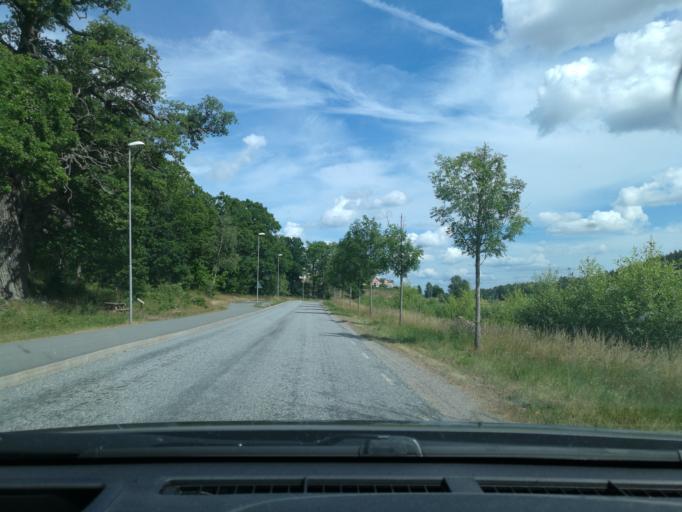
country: SE
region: Stockholm
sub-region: Sigtuna Kommun
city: Marsta
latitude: 59.6059
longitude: 17.8171
